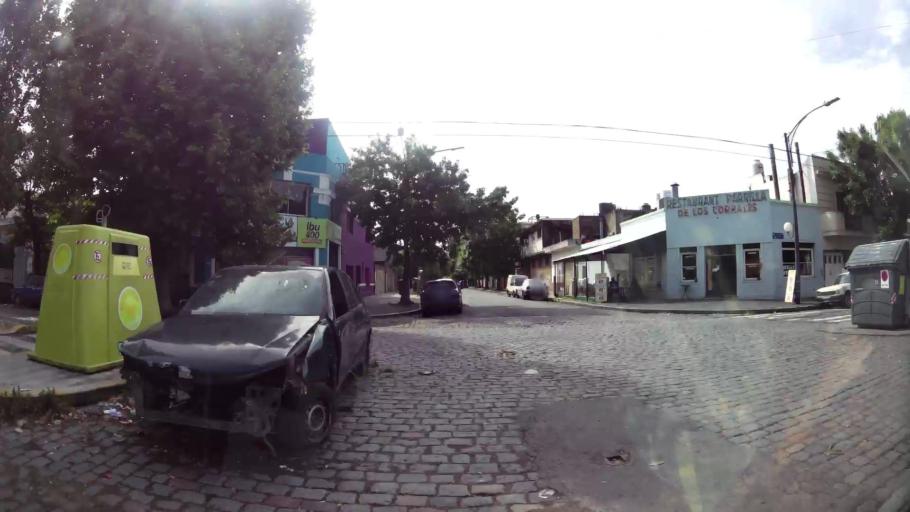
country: AR
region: Buenos Aires F.D.
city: Villa Lugano
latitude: -34.6645
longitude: -58.5026
